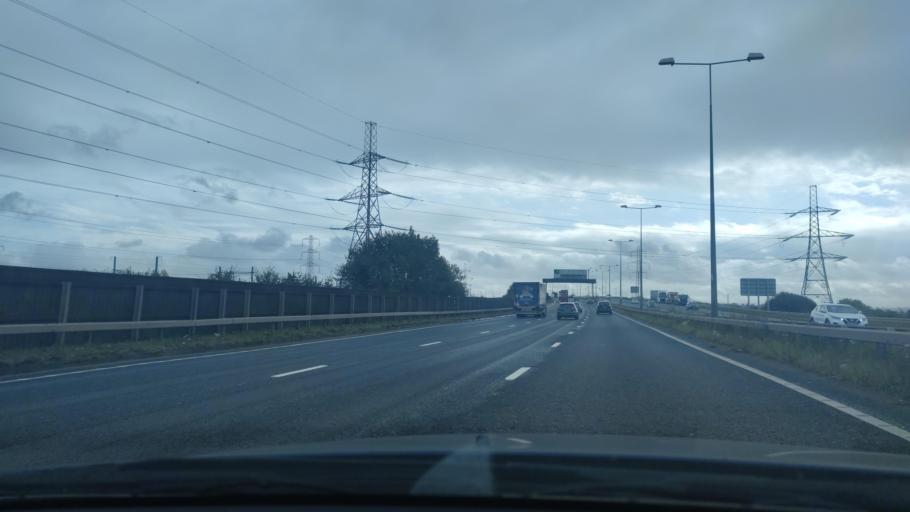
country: GB
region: England
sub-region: Greater London
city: Erith
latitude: 51.5047
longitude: 0.2083
